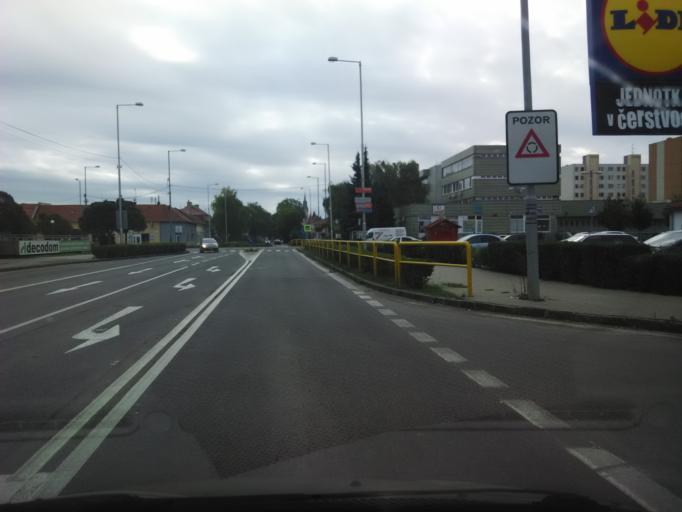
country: SK
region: Nitriansky
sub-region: Okres Nitra
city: Vrable
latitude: 48.2449
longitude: 18.3039
